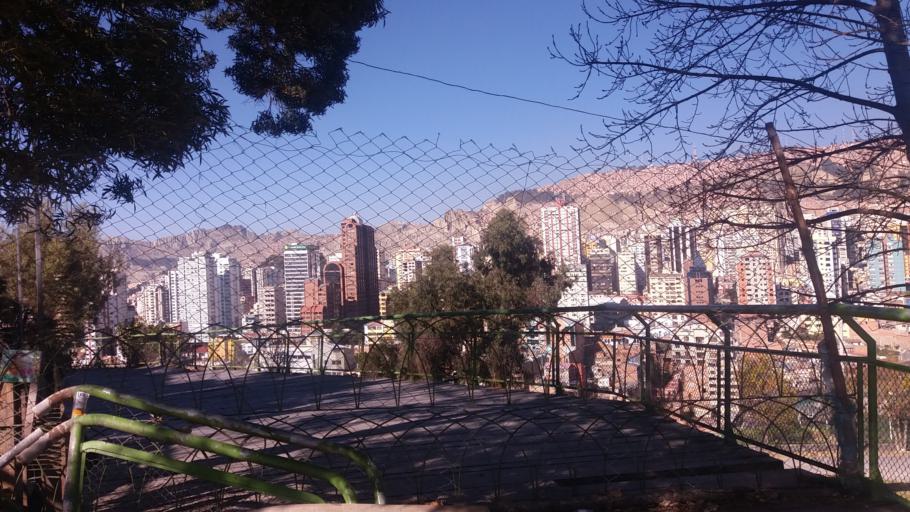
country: BO
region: La Paz
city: La Paz
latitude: -16.5026
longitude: -68.1247
